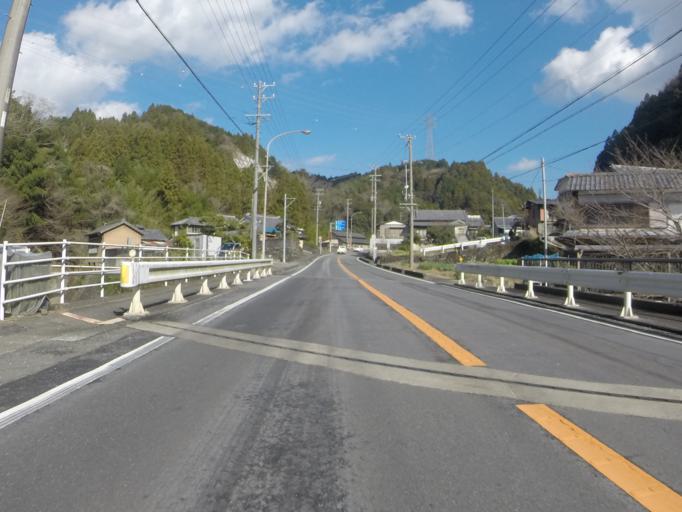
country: JP
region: Shizuoka
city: Fujinomiya
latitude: 35.1288
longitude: 138.5155
